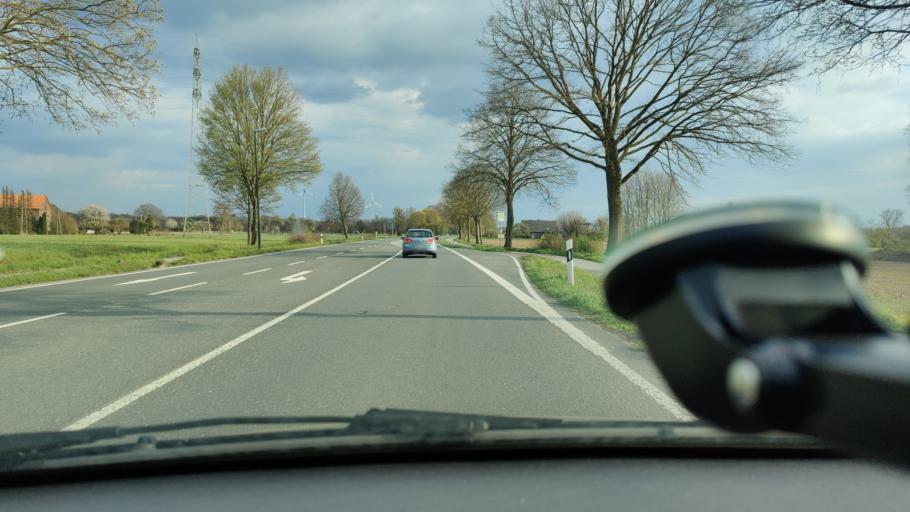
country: DE
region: North Rhine-Westphalia
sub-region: Regierungsbezirk Dusseldorf
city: Hamminkeln
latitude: 51.7200
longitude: 6.5951
